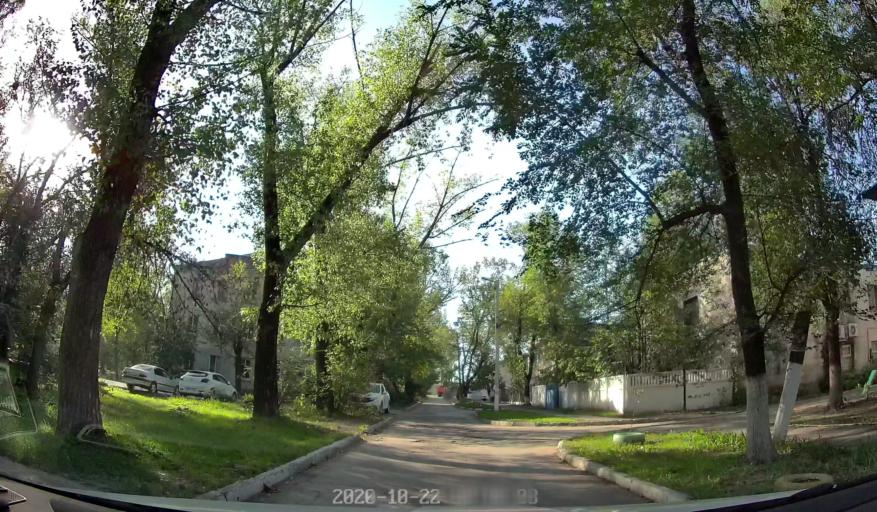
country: MD
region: Chisinau
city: Singera
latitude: 46.9394
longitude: 28.9262
